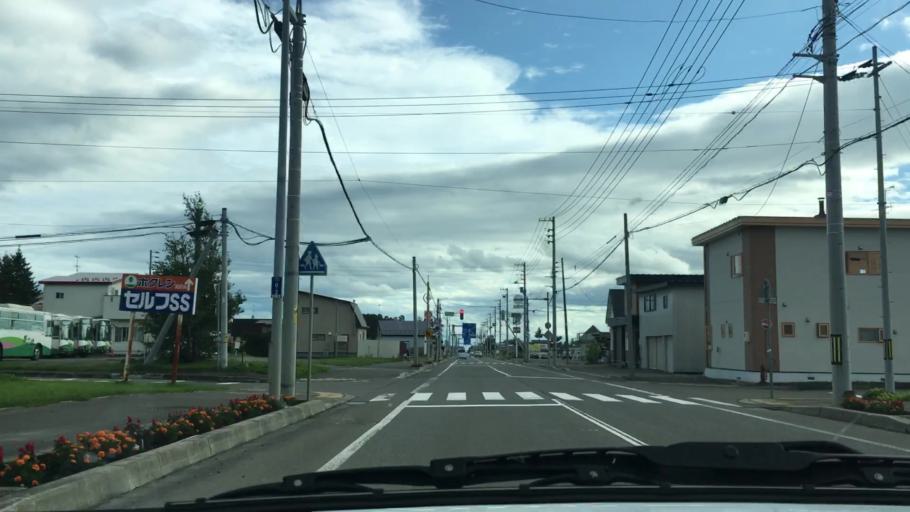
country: JP
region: Hokkaido
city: Otofuke
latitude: 43.2301
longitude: 143.2945
